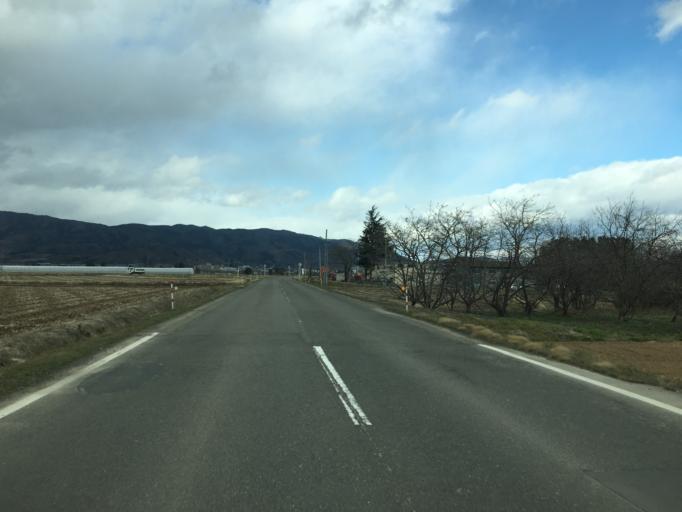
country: JP
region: Fukushima
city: Hobaramachi
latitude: 37.8538
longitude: 140.5341
